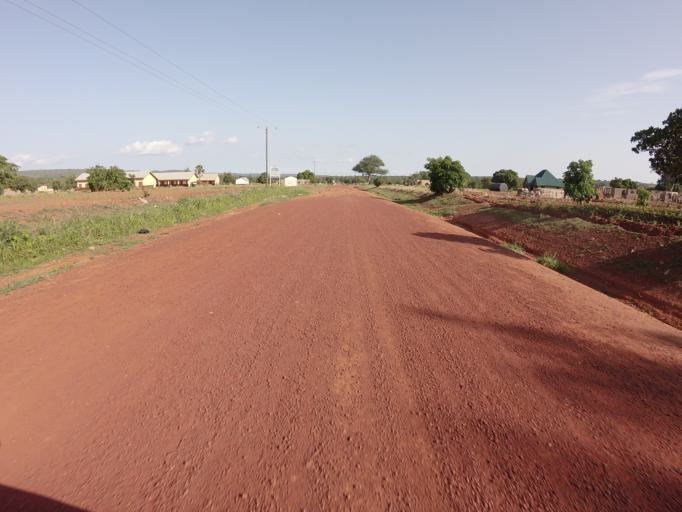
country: GH
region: Upper East
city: Bawku
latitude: 10.6251
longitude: -0.1790
